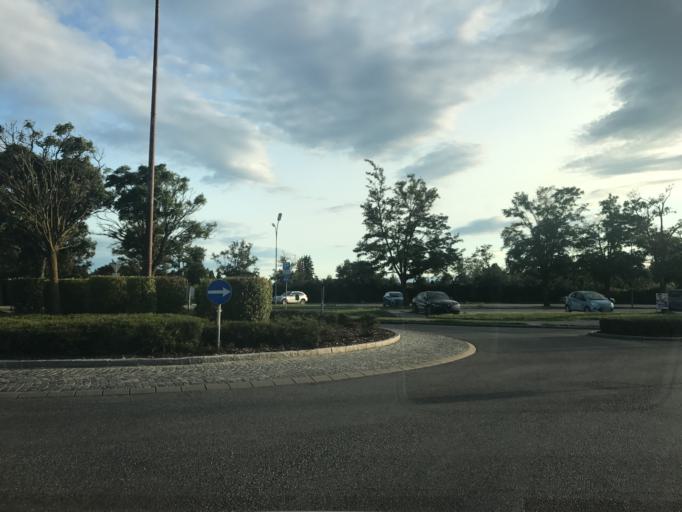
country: AT
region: Lower Austria
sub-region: Politischer Bezirk Wiener Neustadt
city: Theresienfeld
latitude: 47.8292
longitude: 16.2473
